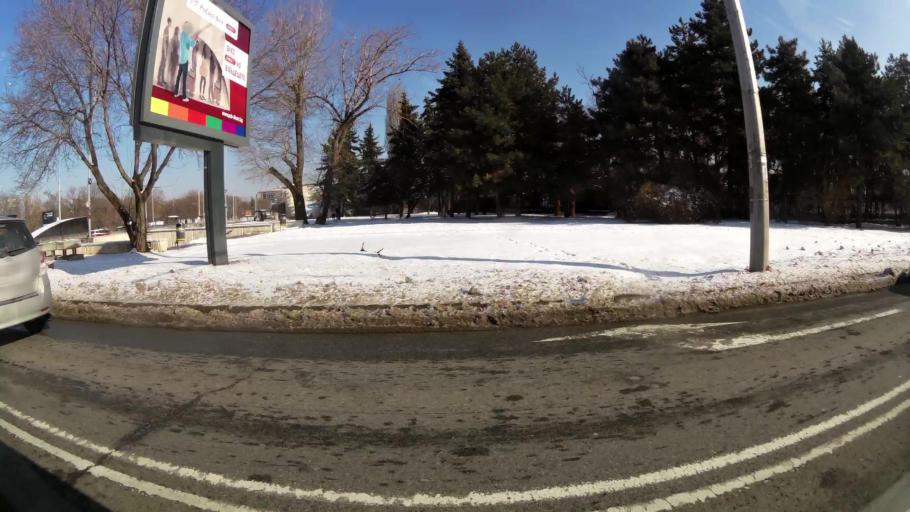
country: BG
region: Sofia-Capital
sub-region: Stolichna Obshtina
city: Sofia
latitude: 42.6789
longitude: 23.3028
